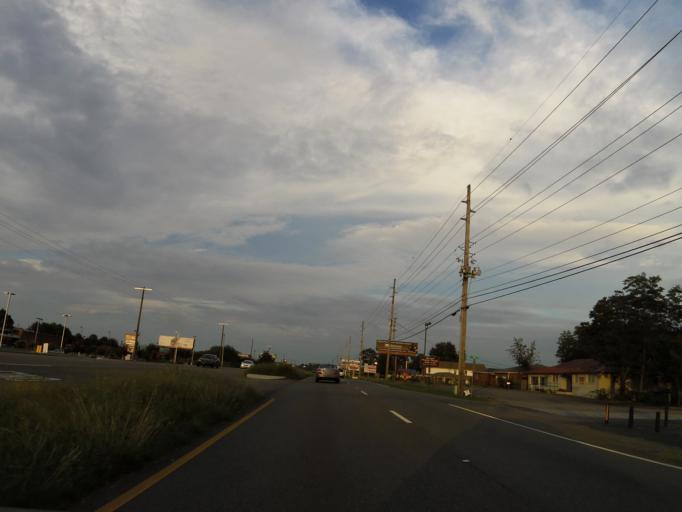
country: US
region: Alabama
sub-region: Madison County
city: Madison
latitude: 34.7545
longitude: -86.7375
